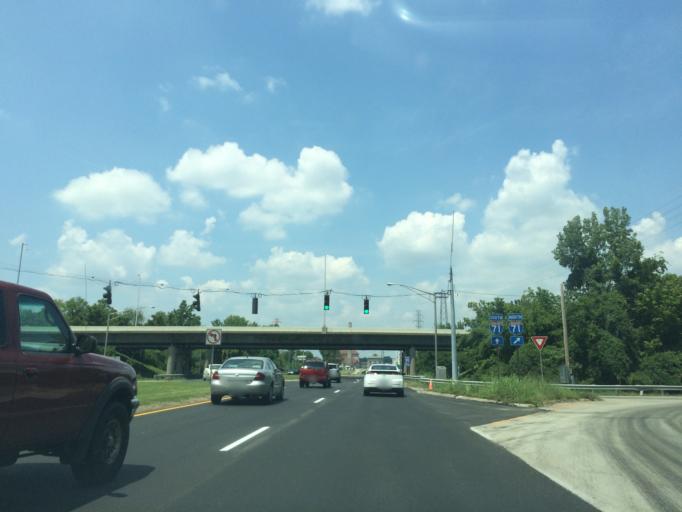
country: US
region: Indiana
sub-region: Clark County
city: Oak Park
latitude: 38.2741
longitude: -85.6965
